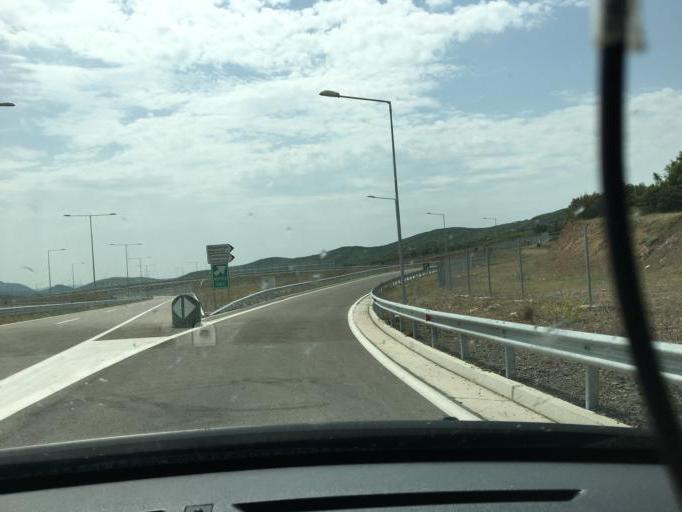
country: MK
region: Gevgelija
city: Miravci
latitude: 41.2653
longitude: 22.4695
